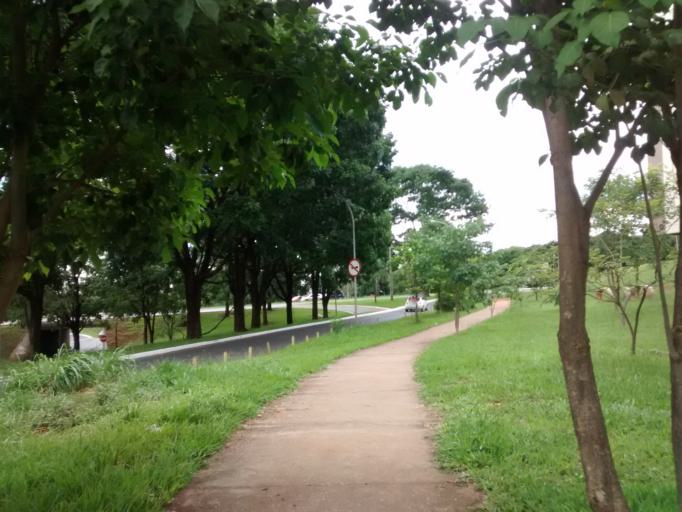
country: BR
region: Federal District
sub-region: Brasilia
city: Brasilia
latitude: -15.7587
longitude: -47.8869
